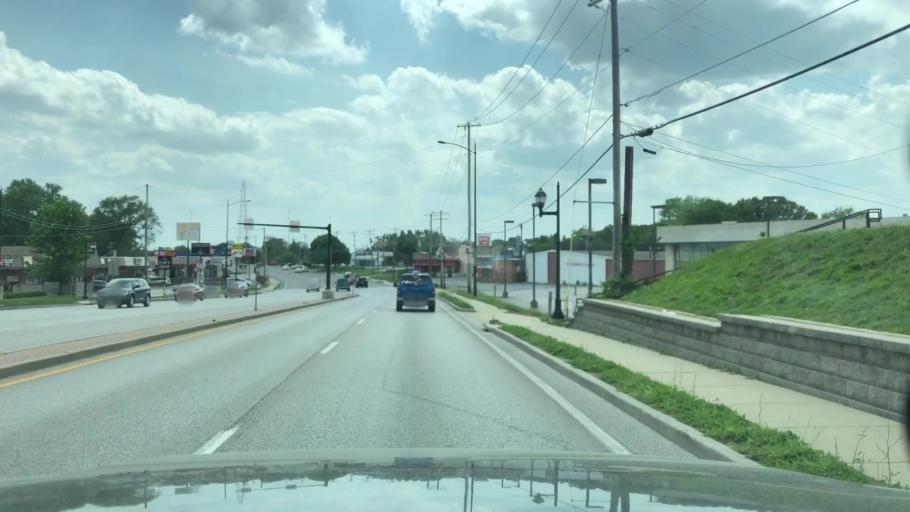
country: US
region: Missouri
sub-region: Saint Charles County
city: Saint Charles
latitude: 38.7821
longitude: -90.5060
